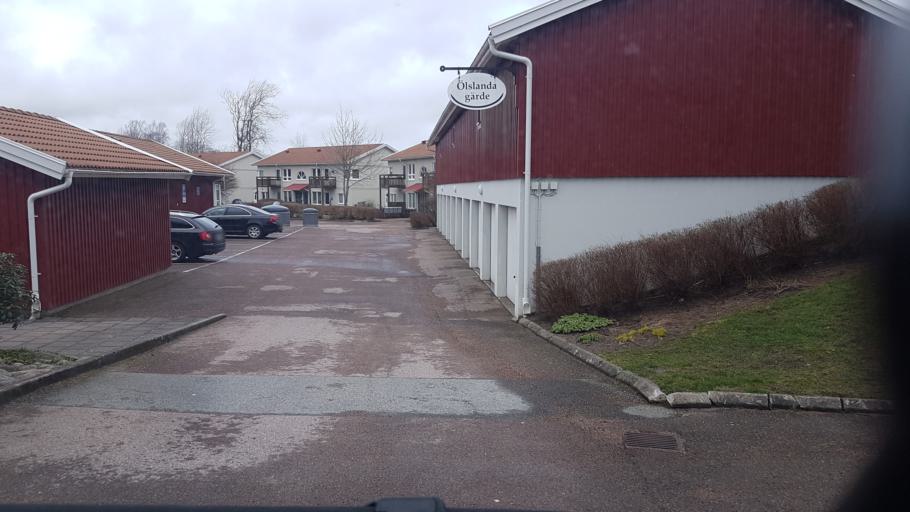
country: SE
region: Vaestra Goetaland
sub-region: Lerums Kommun
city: Stenkullen
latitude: 57.7885
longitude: 12.3021
